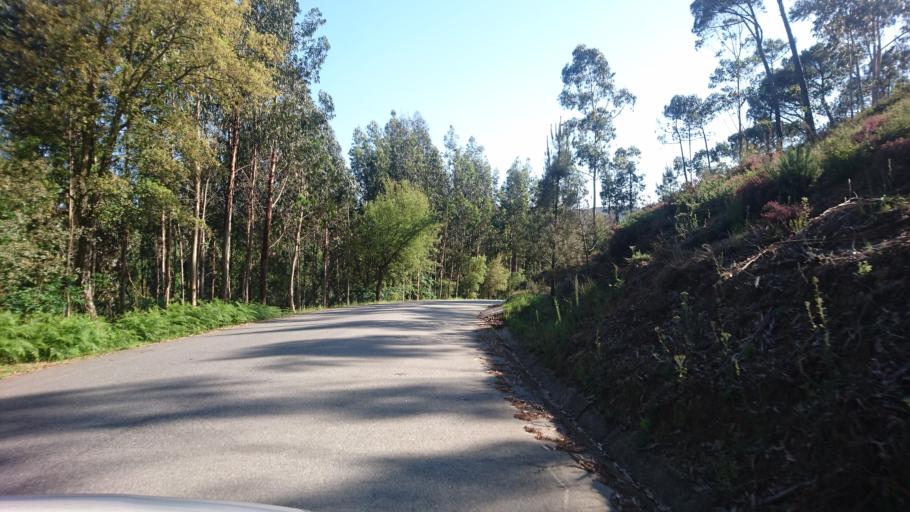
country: PT
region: Porto
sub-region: Paredes
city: Recarei
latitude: 41.1523
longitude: -8.3853
